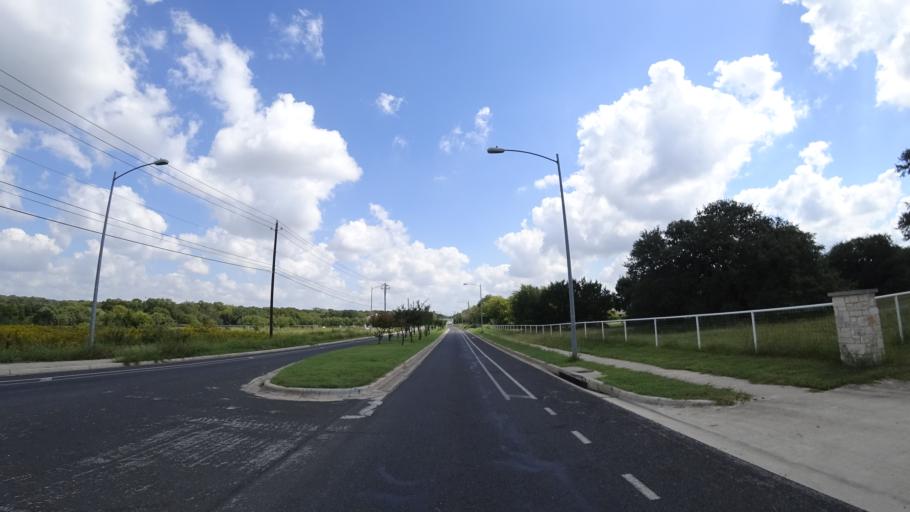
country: US
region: Texas
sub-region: Travis County
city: Manchaca
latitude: 30.1856
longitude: -97.8083
